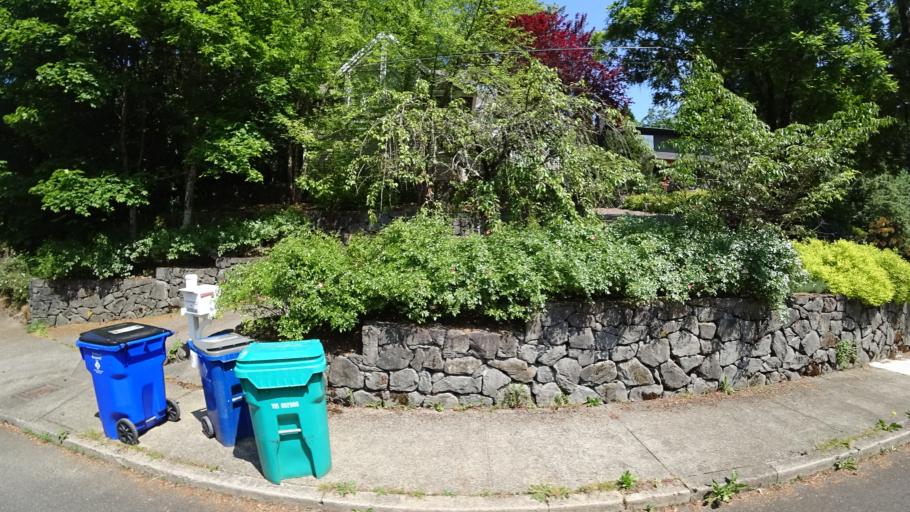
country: US
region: Oregon
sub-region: Multnomah County
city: Portland
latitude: 45.4945
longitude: -122.7034
